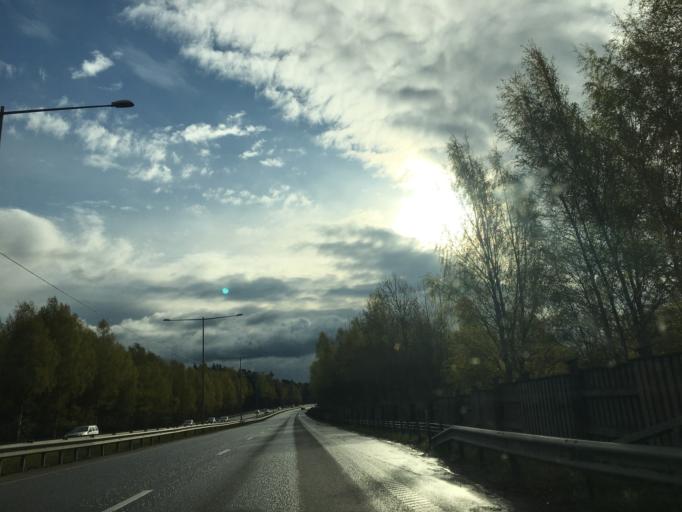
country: SE
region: Vaermland
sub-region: Karlstads Kommun
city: Karlstad
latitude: 59.4001
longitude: 13.5398
